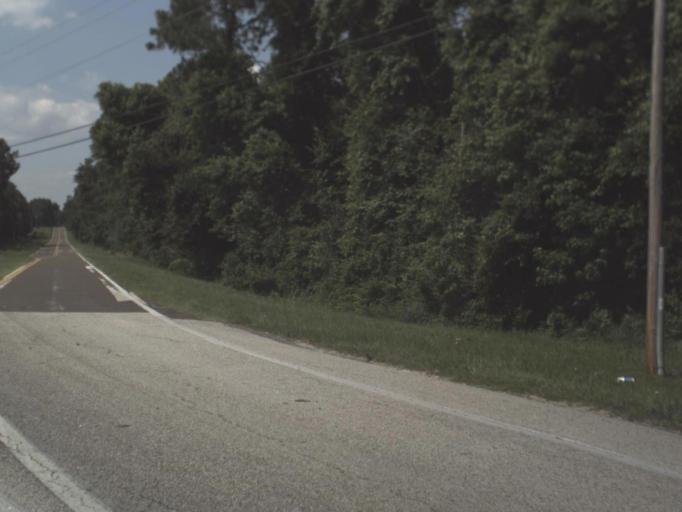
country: US
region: Florida
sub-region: Alachua County
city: Hawthorne
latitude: 29.6207
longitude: -82.0972
